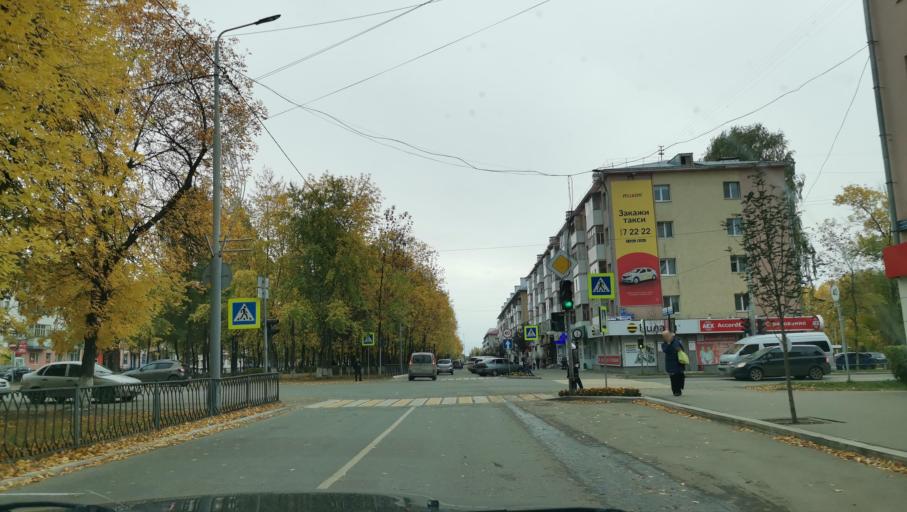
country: RU
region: Bashkortostan
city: Neftekamsk
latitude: 56.0929
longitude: 54.2528
